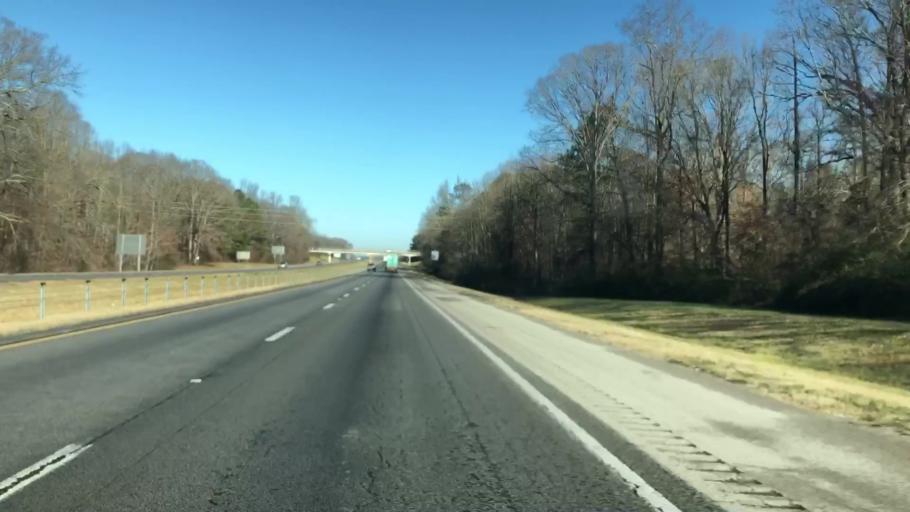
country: US
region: Alabama
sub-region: Limestone County
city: Athens
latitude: 34.7923
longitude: -86.9396
